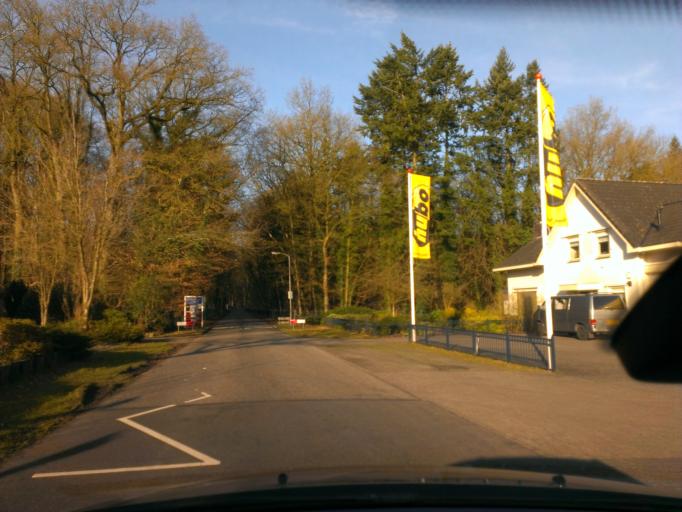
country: NL
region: Gelderland
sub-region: Gemeente Heerde
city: Heerde
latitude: 52.4244
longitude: 6.0667
